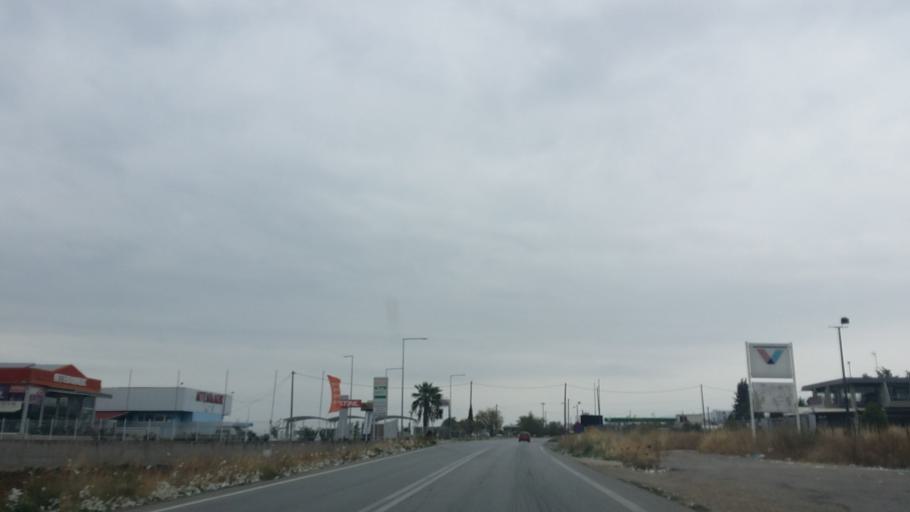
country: GR
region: Central Greece
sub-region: Nomos Voiotias
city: Thivai
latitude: 38.3273
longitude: 23.2826
